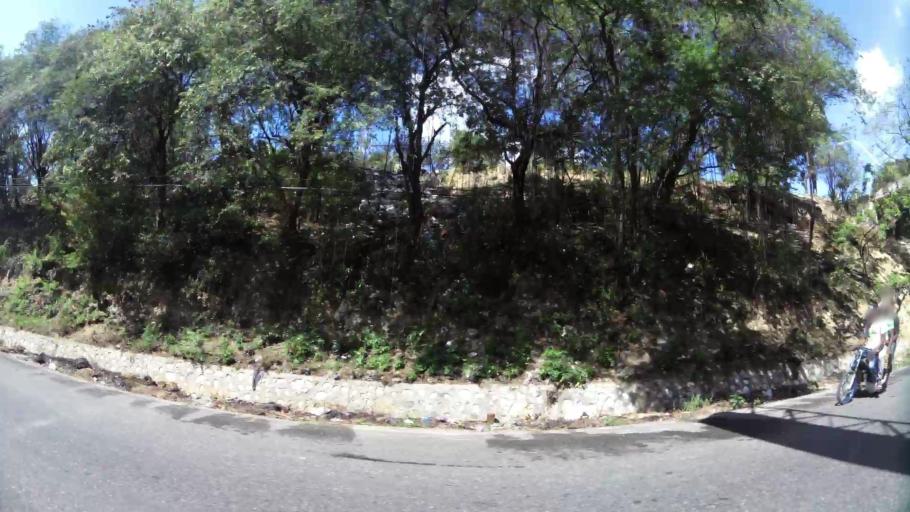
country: DO
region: San Cristobal
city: San Cristobal
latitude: 18.4288
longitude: -70.0839
